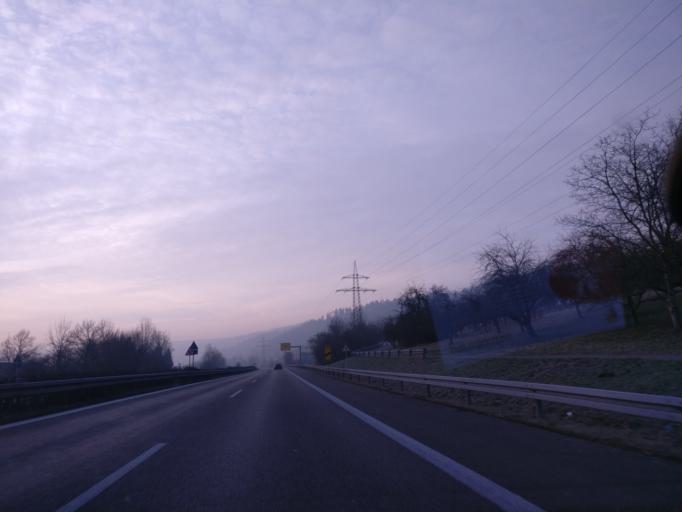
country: DE
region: Baden-Wuerttemberg
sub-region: Regierungsbezirk Stuttgart
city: Pluderhausen
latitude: 48.7953
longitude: 9.5856
